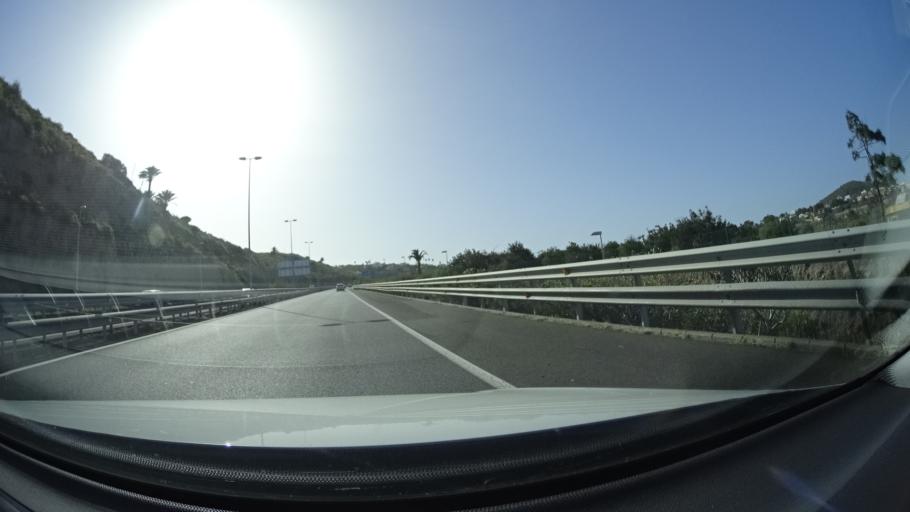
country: ES
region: Canary Islands
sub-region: Provincia de Las Palmas
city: Santa Brigida
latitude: 28.0498
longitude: -15.4493
